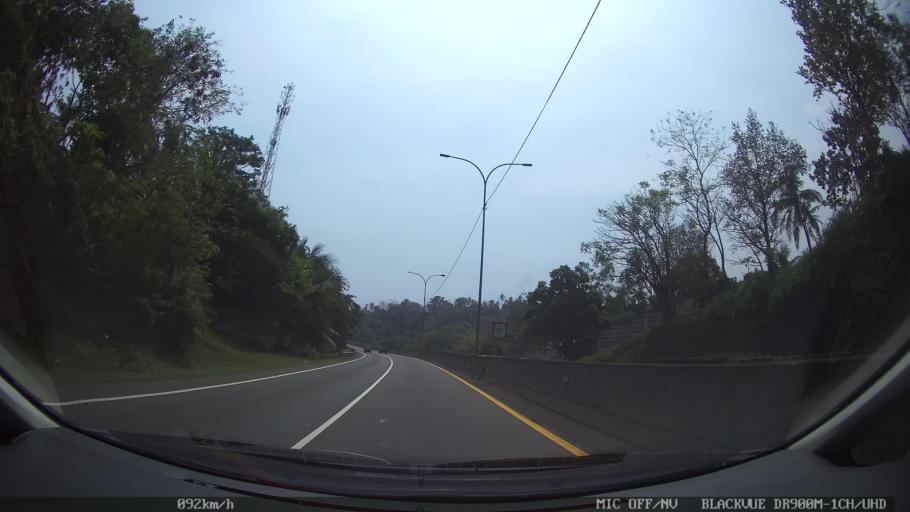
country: ID
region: Banten
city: Curug
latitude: -5.9788
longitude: 106.0184
